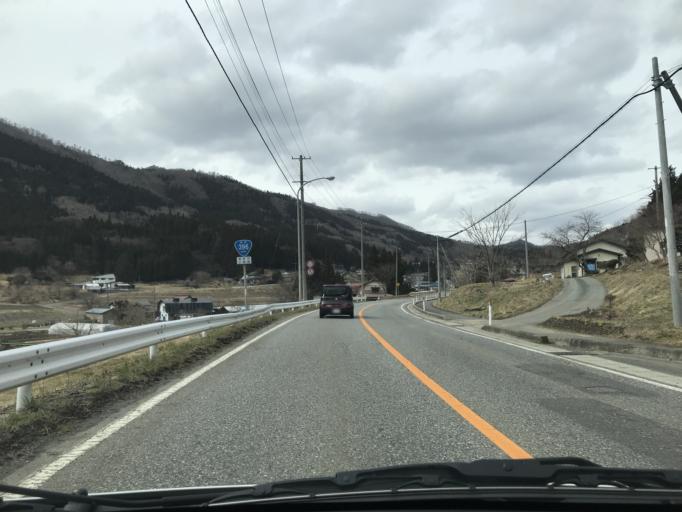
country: JP
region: Iwate
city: Tono
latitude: 39.3351
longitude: 141.4470
